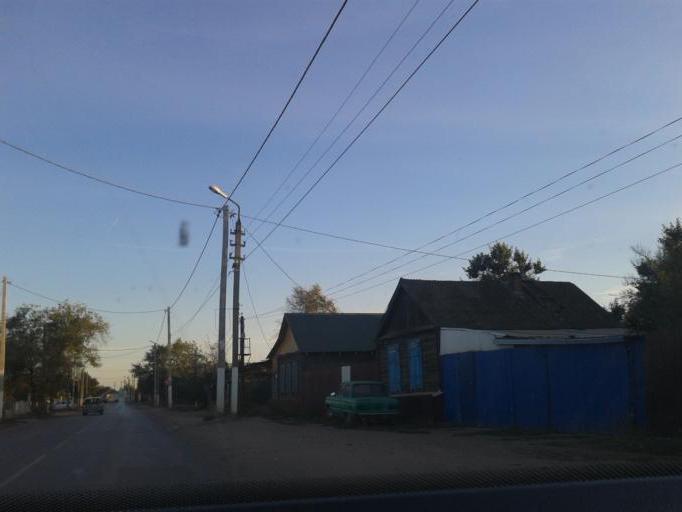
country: RU
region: Volgograd
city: Krasnoslobodsk
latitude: 48.7062
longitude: 44.5651
